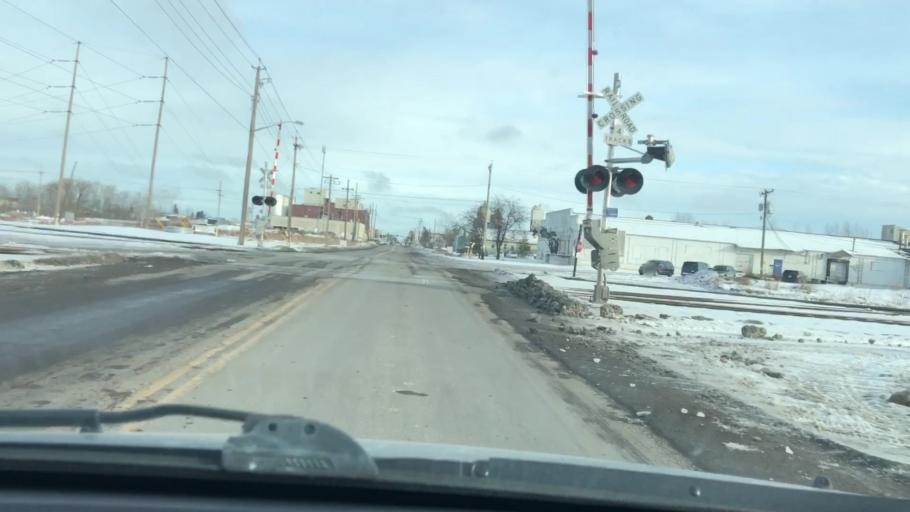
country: US
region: Wisconsin
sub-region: Douglas County
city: Superior
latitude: 46.7279
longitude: -92.1115
